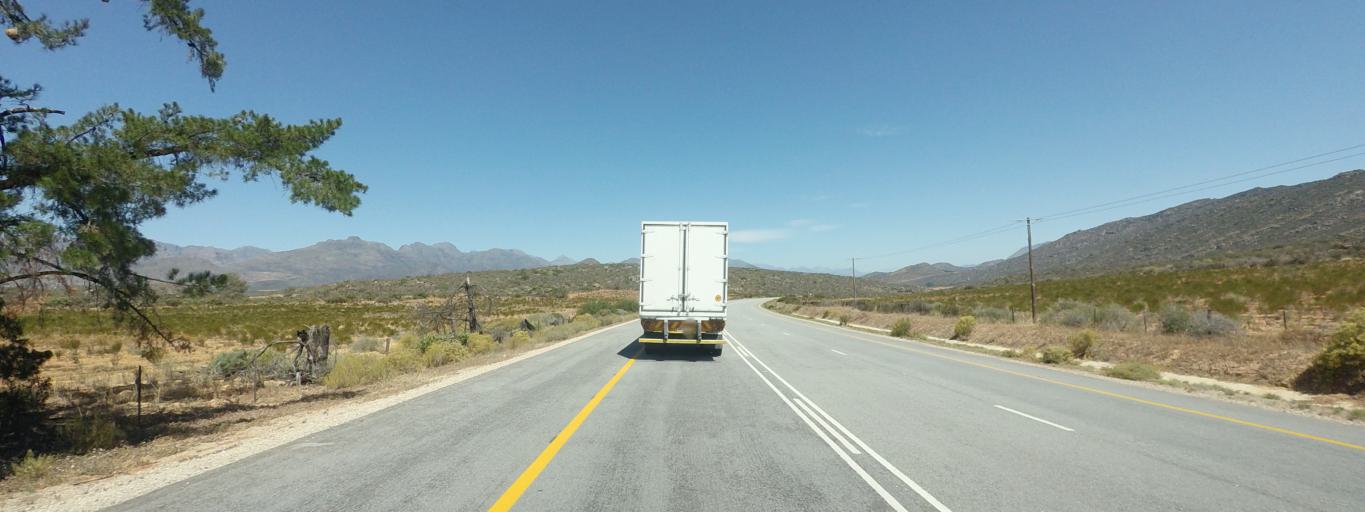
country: ZA
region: Western Cape
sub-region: West Coast District Municipality
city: Clanwilliam
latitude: -32.3274
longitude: 18.9223
